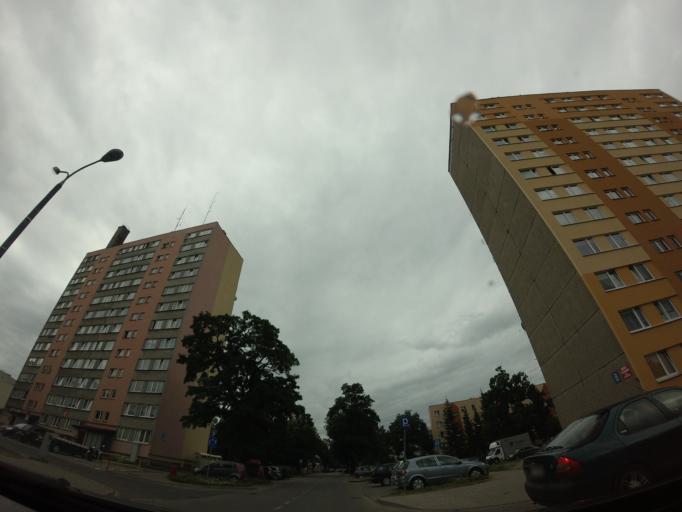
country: PL
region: Masovian Voivodeship
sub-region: Powiat ciechanowski
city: Ciechanow
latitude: 52.8780
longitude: 20.6167
